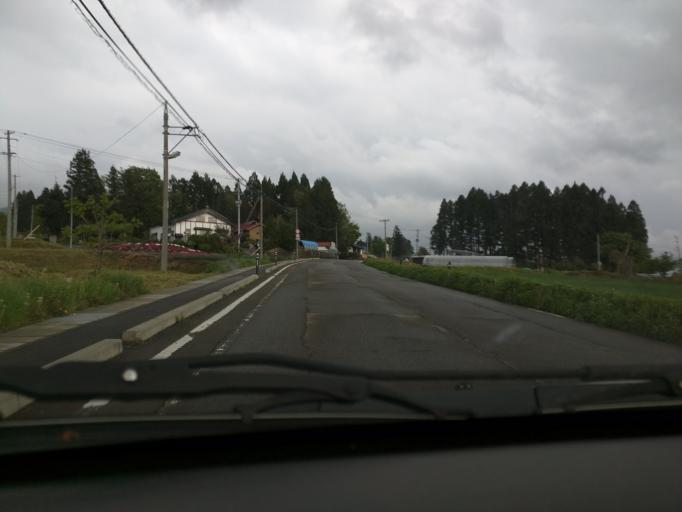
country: JP
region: Fukushima
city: Kitakata
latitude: 37.6319
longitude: 139.9351
